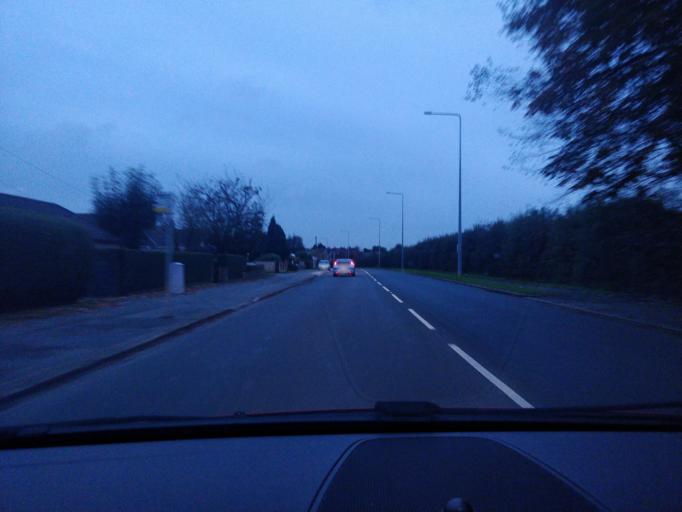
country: GB
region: England
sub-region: Lancashire
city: Ormskirk
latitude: 53.5763
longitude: -2.8947
